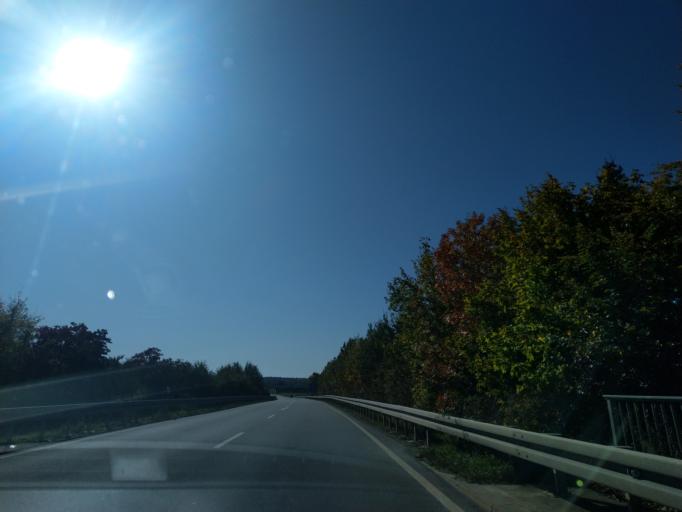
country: DE
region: Bavaria
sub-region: Lower Bavaria
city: Plattling
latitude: 48.8019
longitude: 12.9034
